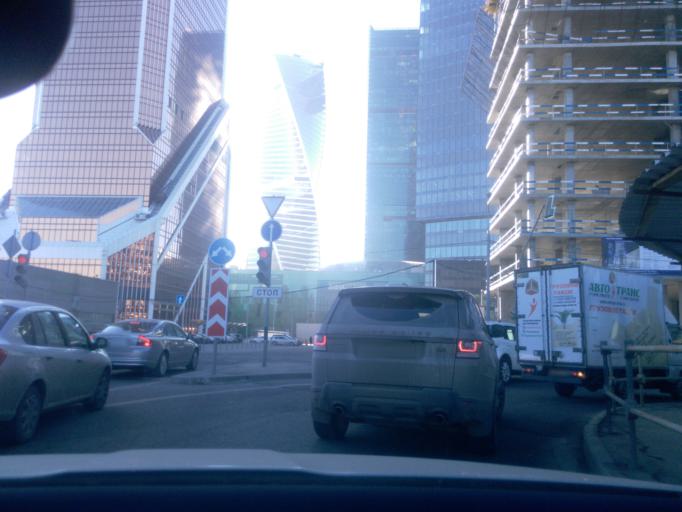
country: RU
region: Moskovskaya
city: Presnenskiy
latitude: 55.7514
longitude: 37.5370
